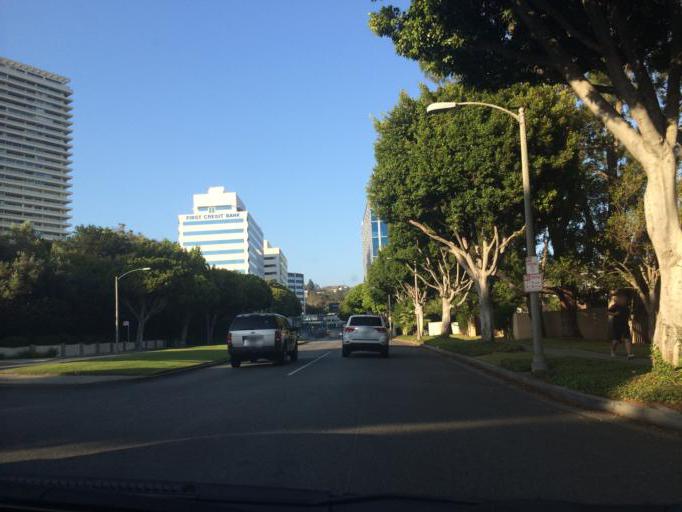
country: US
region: California
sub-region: Los Angeles County
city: Beverly Hills
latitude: 34.0885
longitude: -118.3956
